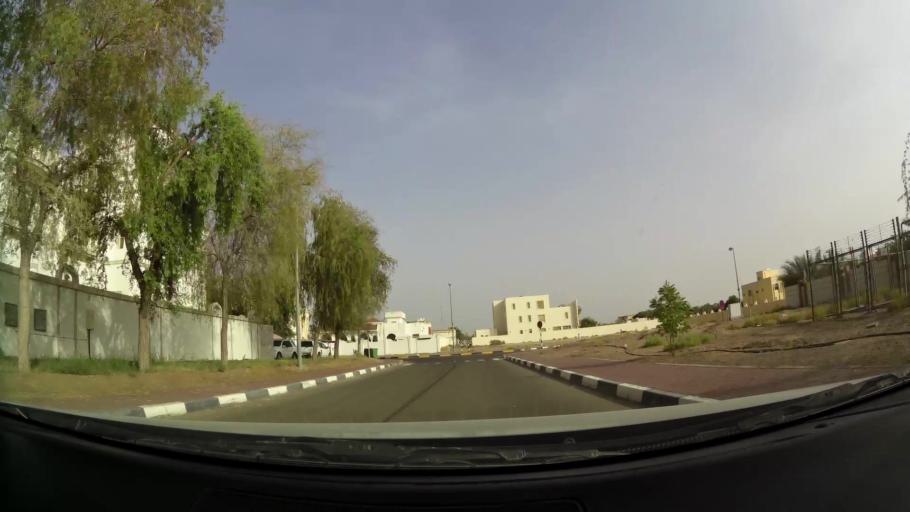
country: AE
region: Abu Dhabi
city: Al Ain
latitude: 24.2265
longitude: 55.6669
